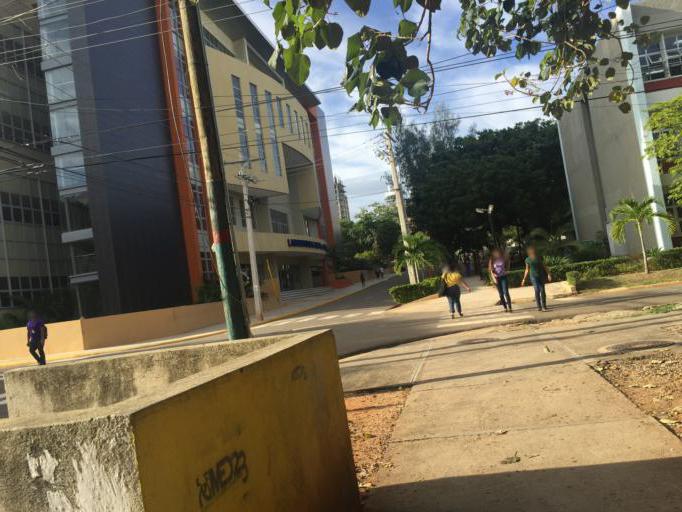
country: DO
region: Nacional
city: La Julia
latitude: 18.4621
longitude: -69.9173
